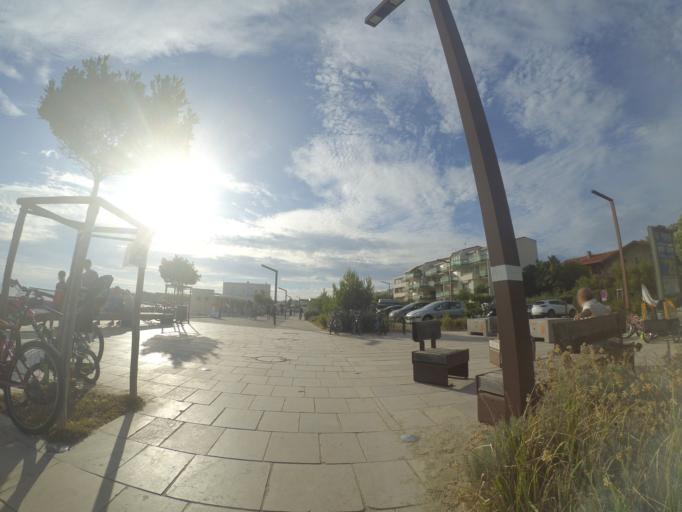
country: FR
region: Poitou-Charentes
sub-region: Departement de la Charente-Maritime
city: Saint-Georges-de-Didonne
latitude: 45.6004
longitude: -0.9964
